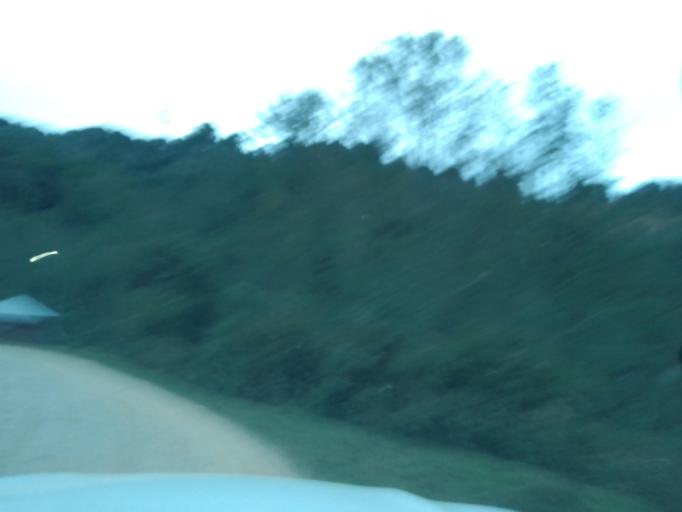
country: MX
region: Chiapas
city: Motozintla de Mendoza
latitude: 15.2167
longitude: -92.2388
